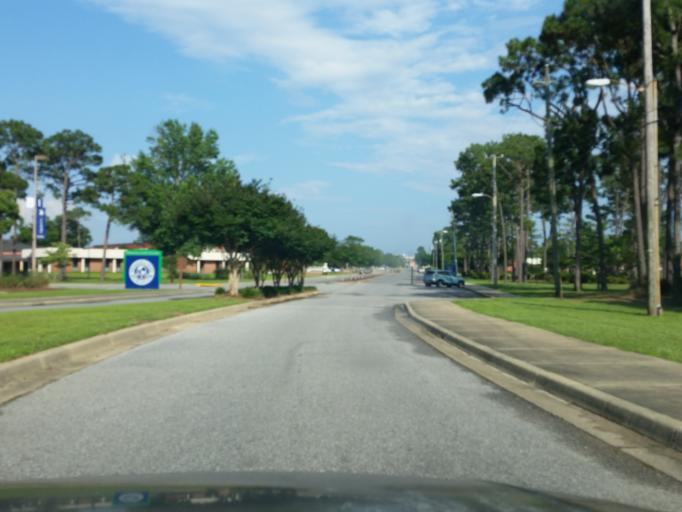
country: US
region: Florida
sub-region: Escambia County
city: Ferry Pass
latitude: 30.4796
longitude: -87.2026
